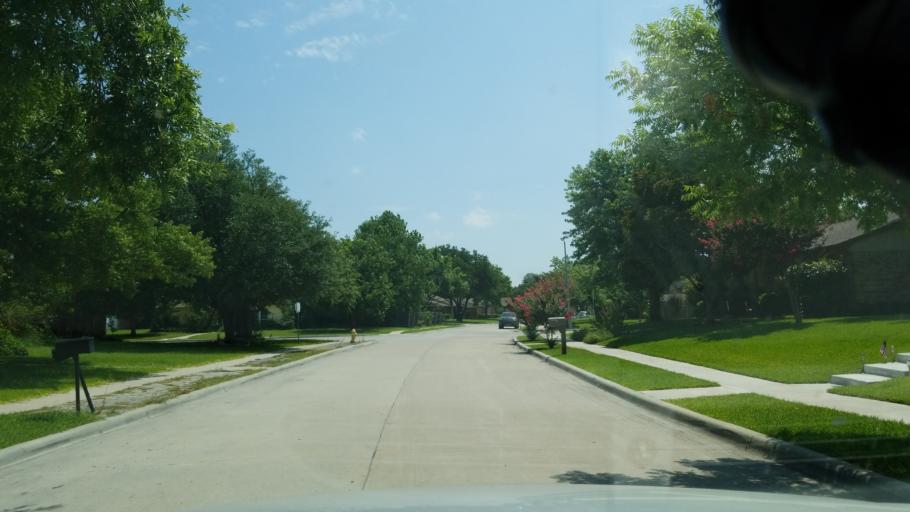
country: US
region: Texas
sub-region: Dallas County
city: Coppell
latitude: 32.9646
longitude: -96.9820
